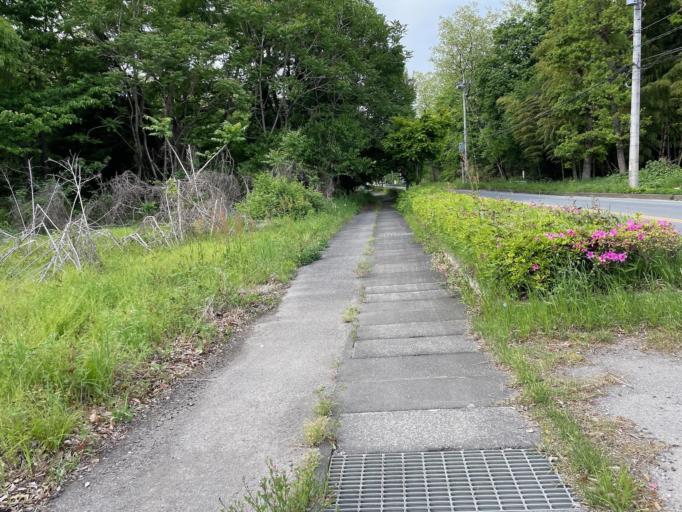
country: JP
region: Tochigi
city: Mibu
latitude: 36.3976
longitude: 139.8034
